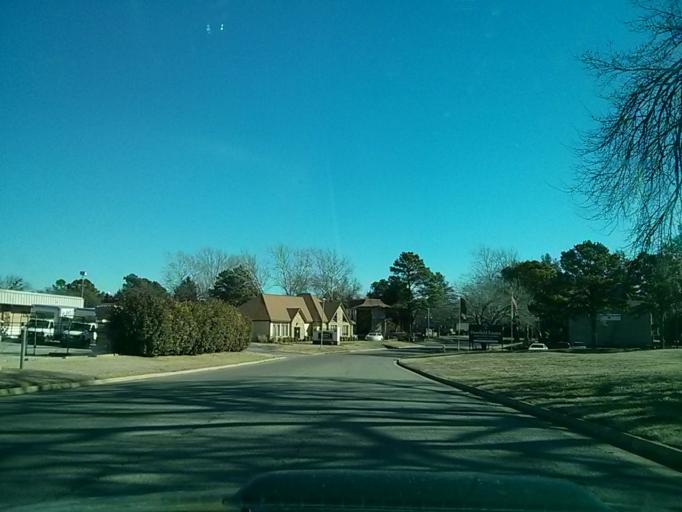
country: US
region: Oklahoma
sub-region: Tulsa County
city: Jenks
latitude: 36.0359
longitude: -95.9541
